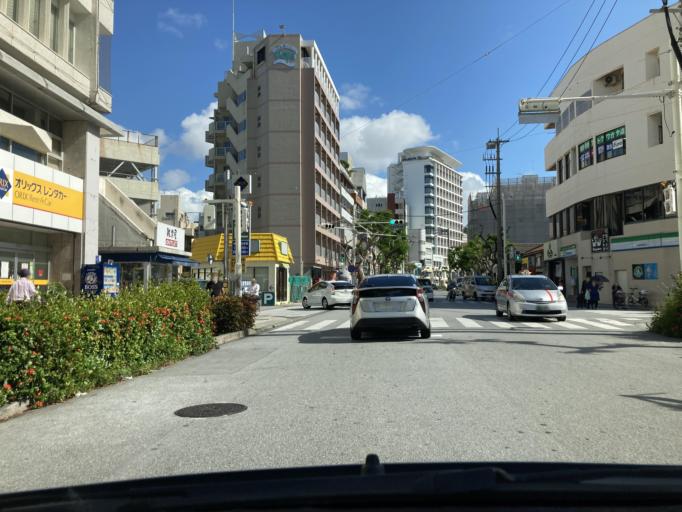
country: JP
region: Okinawa
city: Naha-shi
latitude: 26.2187
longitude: 127.6862
